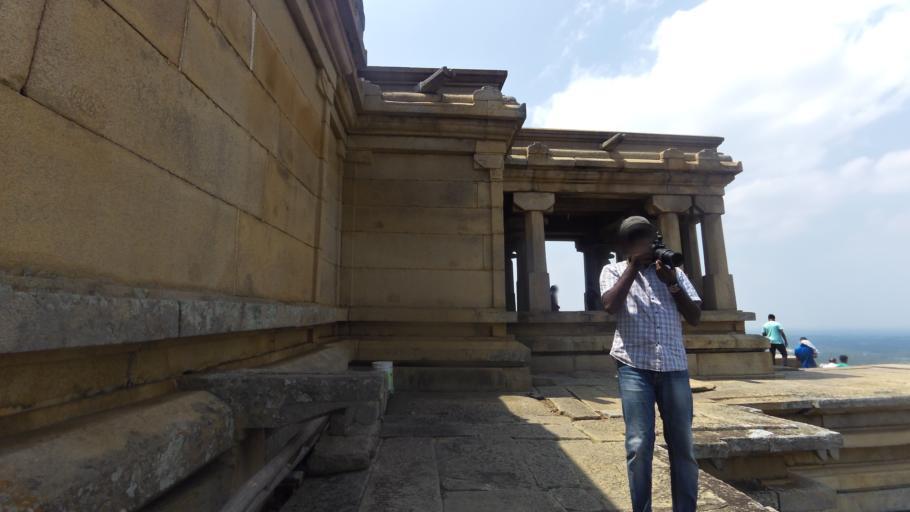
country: IN
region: Karnataka
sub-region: Hassan
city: Shravanabelagola
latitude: 12.8550
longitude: 76.4852
